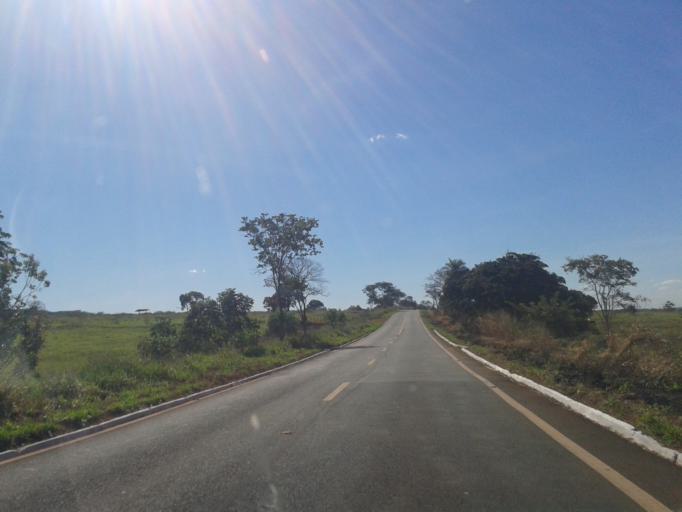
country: BR
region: Minas Gerais
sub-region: Ituiutaba
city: Ituiutaba
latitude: -19.1667
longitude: -49.7799
